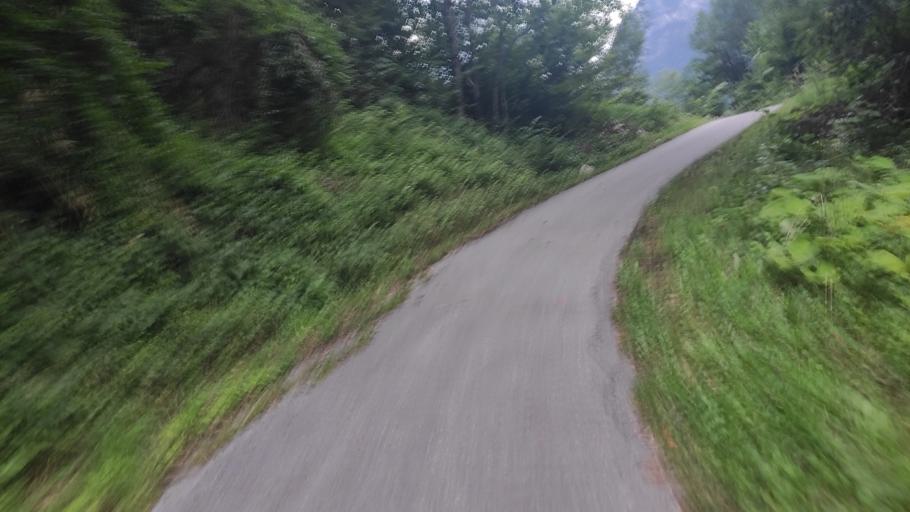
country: AT
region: Salzburg
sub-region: Politischer Bezirk Zell am See
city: Leogang
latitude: 47.5032
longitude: 12.7836
